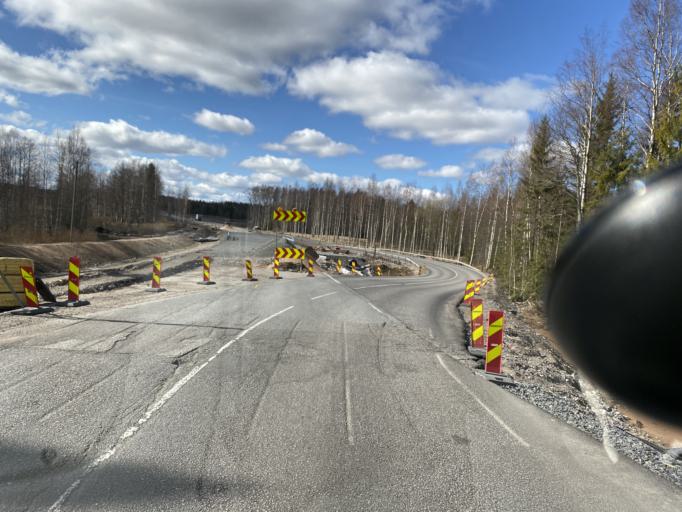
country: FI
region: Satakunta
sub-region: Rauma
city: Koeylioe
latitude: 61.1627
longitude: 22.3119
